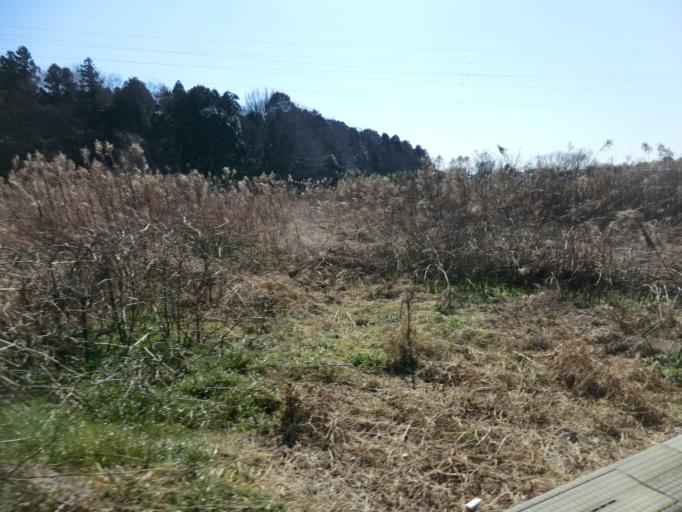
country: JP
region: Ibaraki
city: Naka
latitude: 36.0478
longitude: 140.1186
